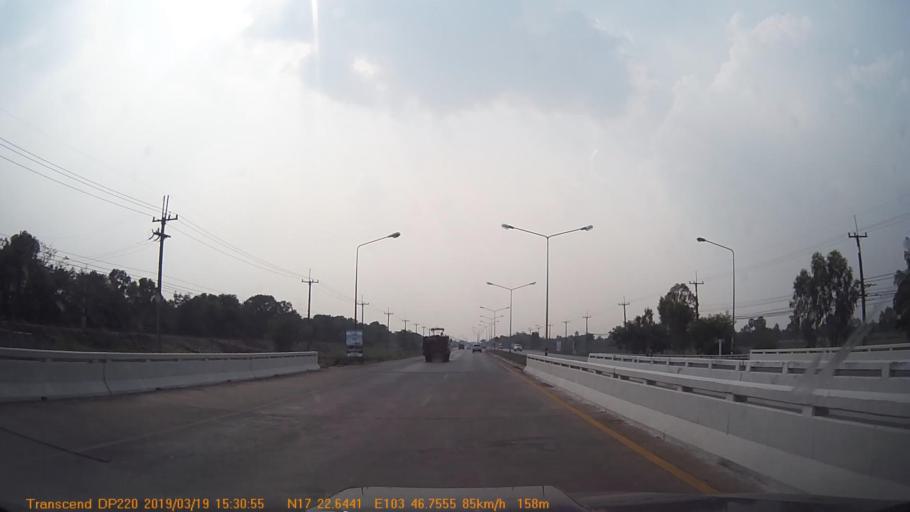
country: TH
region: Sakon Nakhon
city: Phang Khon
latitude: 17.3774
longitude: 103.7789
